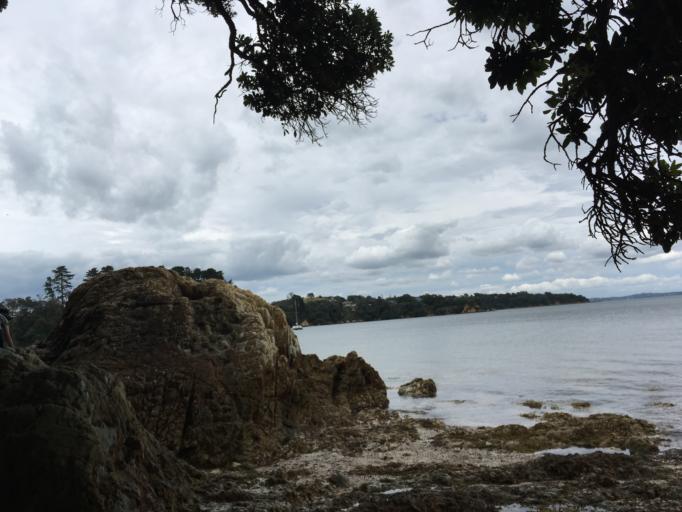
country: NZ
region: Auckland
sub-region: Auckland
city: Pakuranga
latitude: -36.7956
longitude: 175.0257
